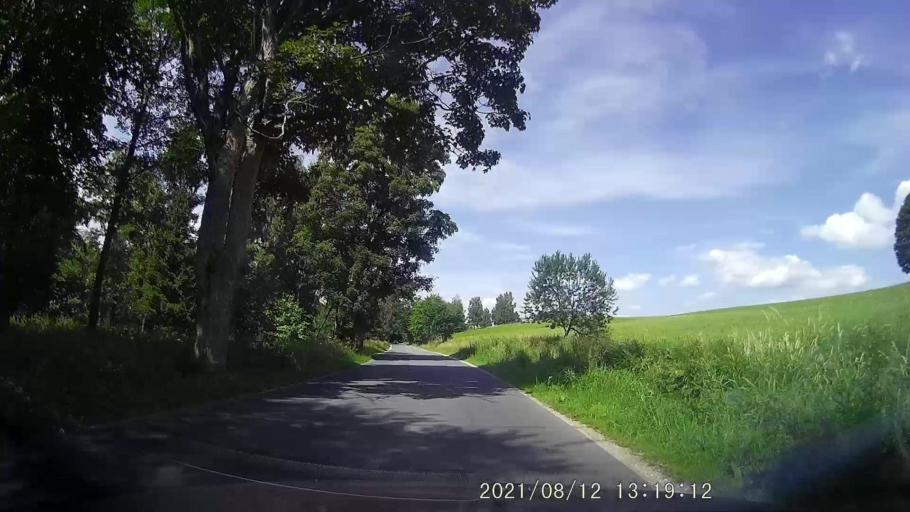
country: PL
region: Lower Silesian Voivodeship
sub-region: Powiat klodzki
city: Stronie Slaskie
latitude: 50.2769
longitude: 16.8851
